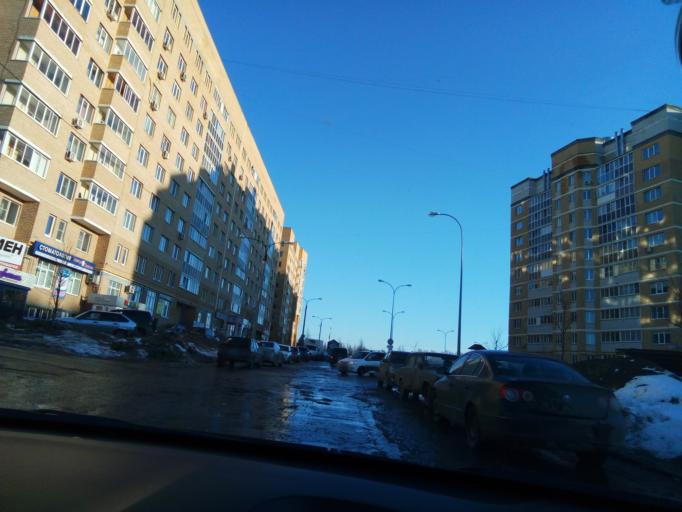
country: RU
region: Chuvashia
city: Novyye Lapsary
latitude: 56.1339
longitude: 47.1587
